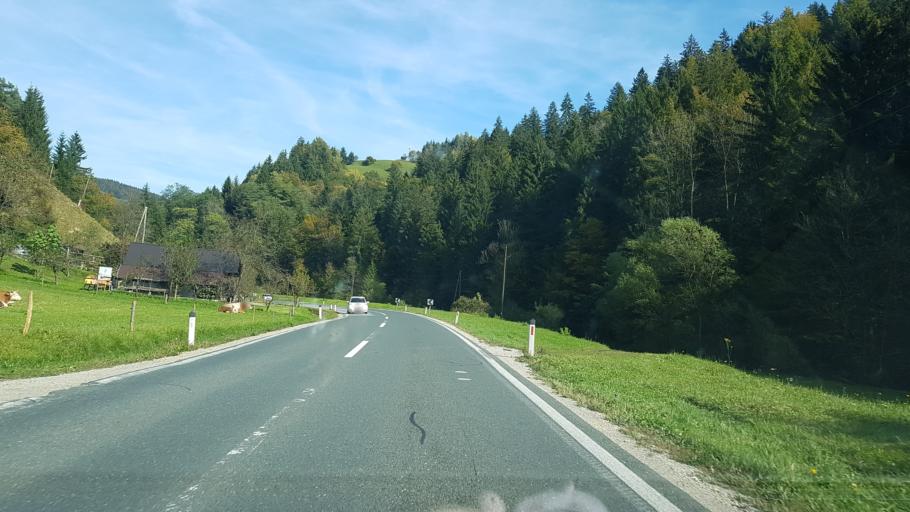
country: SI
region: Velenje
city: Velenje
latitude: 46.3979
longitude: 15.1754
